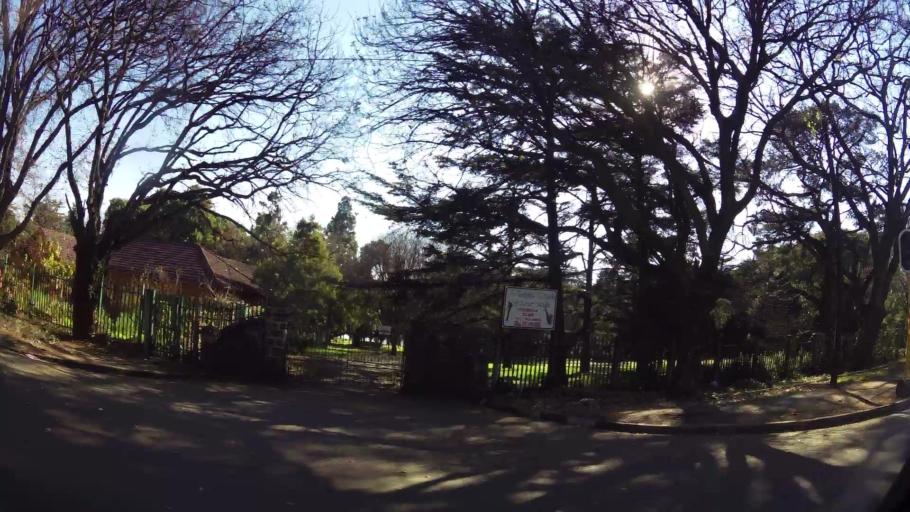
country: ZA
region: Gauteng
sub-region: City of Johannesburg Metropolitan Municipality
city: Johannesburg
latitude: -26.1966
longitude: 28.0950
